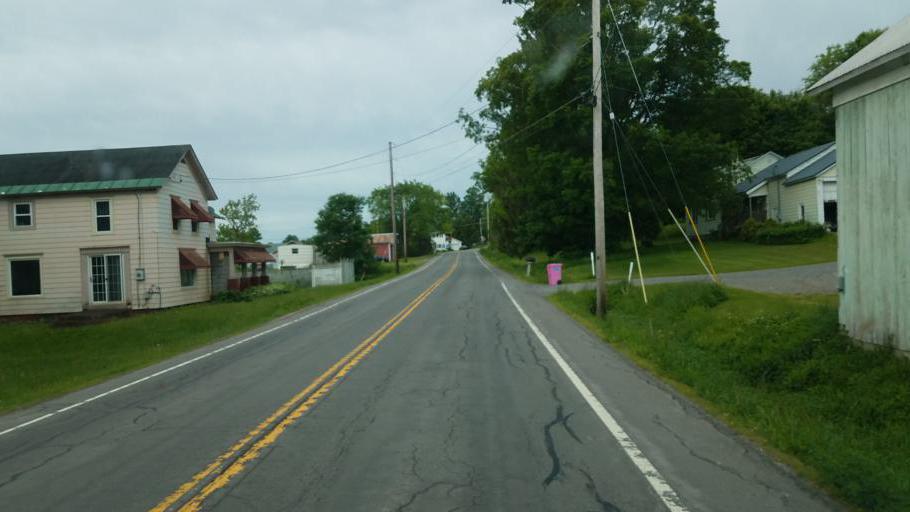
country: US
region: New York
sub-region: Herkimer County
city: Ilion
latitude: 42.9327
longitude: -75.1139
